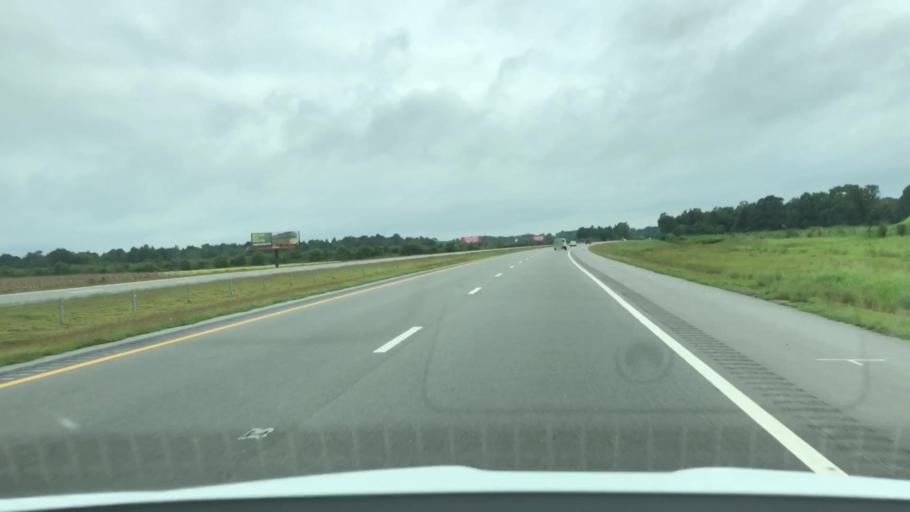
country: US
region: North Carolina
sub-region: Lenoir County
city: La Grange
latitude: 35.3233
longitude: -77.8374
